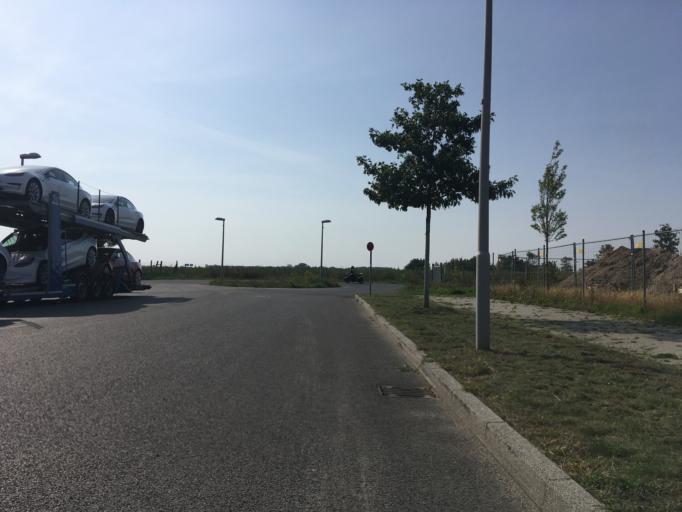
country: DE
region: Brandenburg
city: Schonefeld
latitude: 52.3896
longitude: 13.5370
